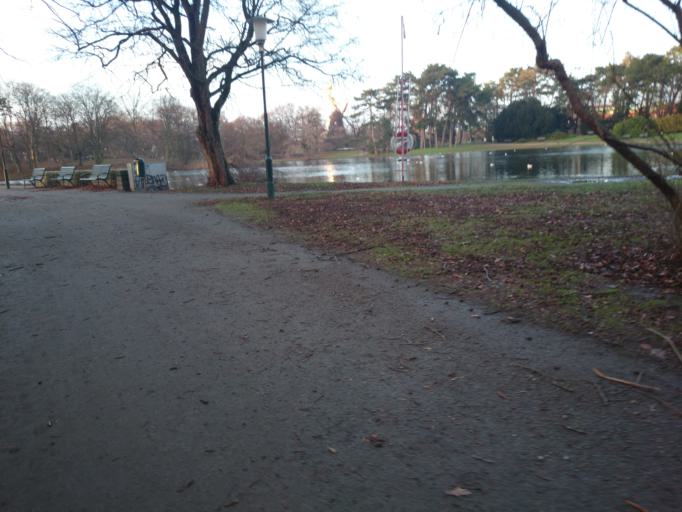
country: SE
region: Skane
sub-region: Malmo
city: Malmoe
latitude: 55.6011
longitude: 12.9879
